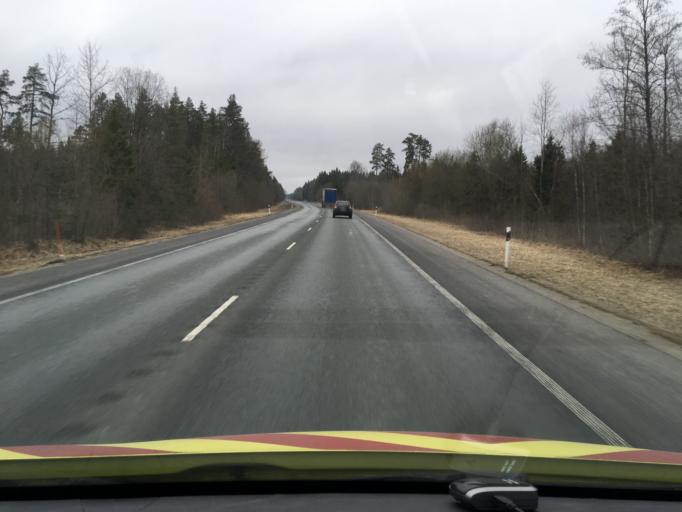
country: EE
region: Raplamaa
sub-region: Kohila vald
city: Kohila
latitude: 59.1411
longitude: 24.7898
